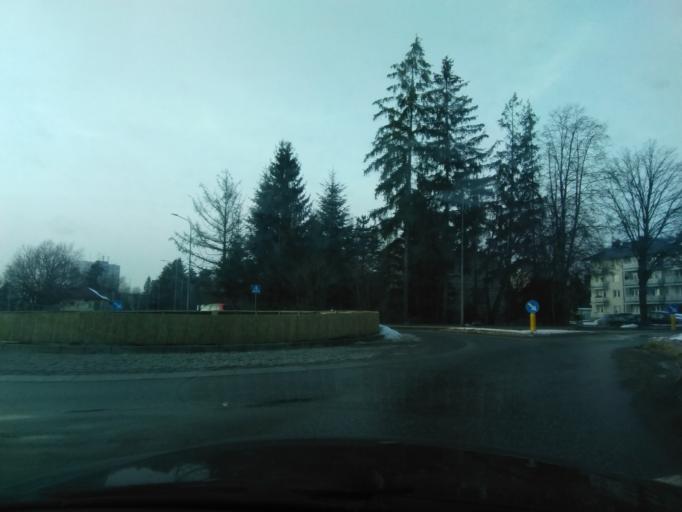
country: PL
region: Subcarpathian Voivodeship
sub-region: Krosno
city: Krosno
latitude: 49.6818
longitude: 21.7751
